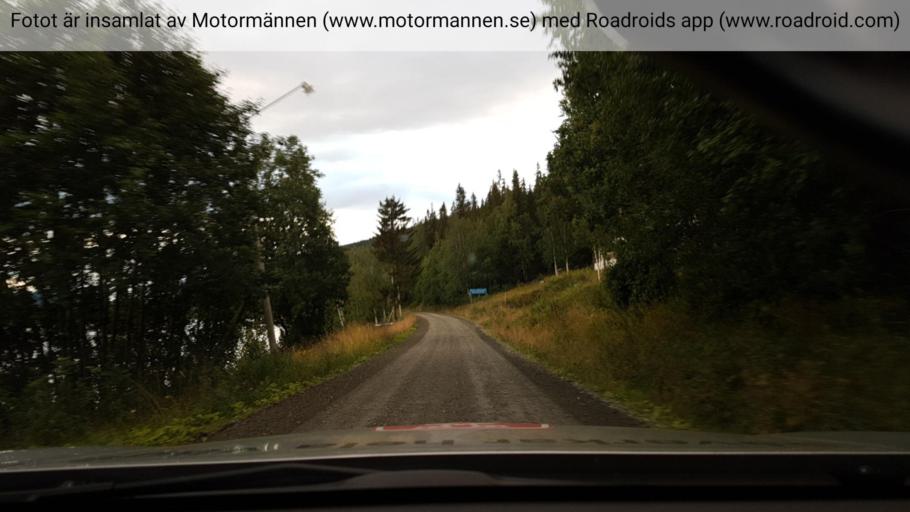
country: NO
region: Nordland
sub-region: Hattfjelldal
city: Hattfjelldal
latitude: 65.6236
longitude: 15.2362
